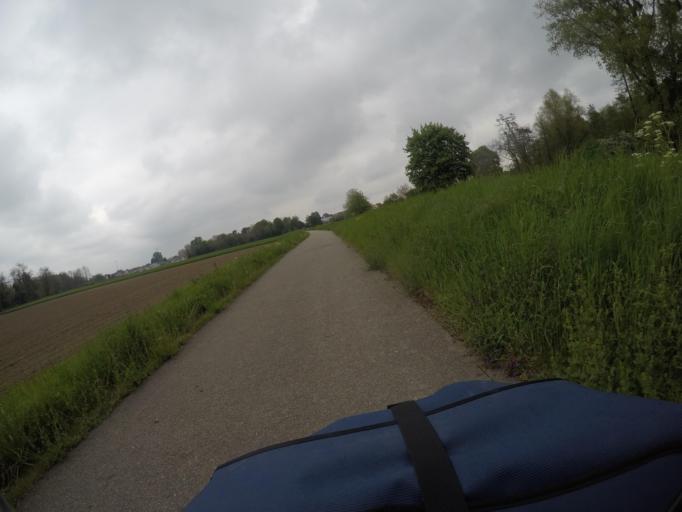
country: FR
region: Alsace
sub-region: Departement du Bas-Rhin
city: Soufflenheim
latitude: 48.8096
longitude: 8.0052
